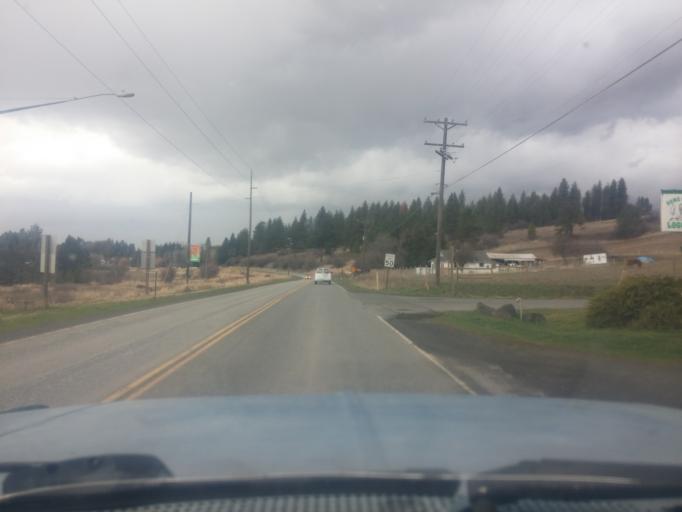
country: US
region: Idaho
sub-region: Latah County
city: Moscow
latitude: 46.9278
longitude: -116.9063
